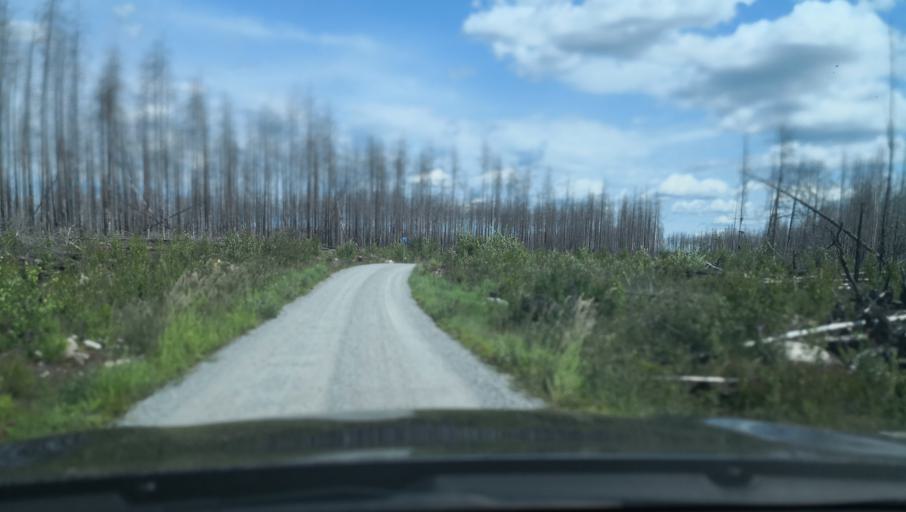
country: SE
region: Vaestmanland
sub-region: Surahammars Kommun
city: Ramnas
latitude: 59.8978
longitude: 16.1166
